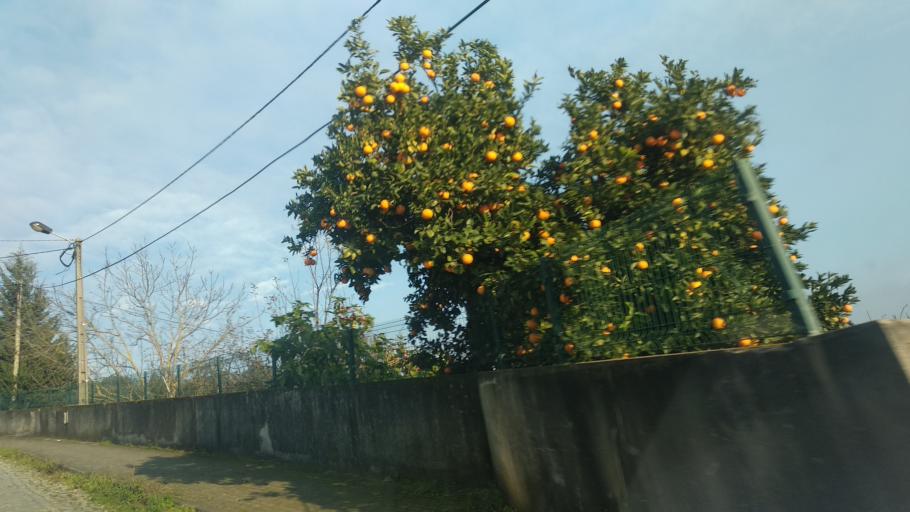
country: PT
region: Braga
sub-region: Braga
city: Adaufe
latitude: 41.5709
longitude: -8.3791
